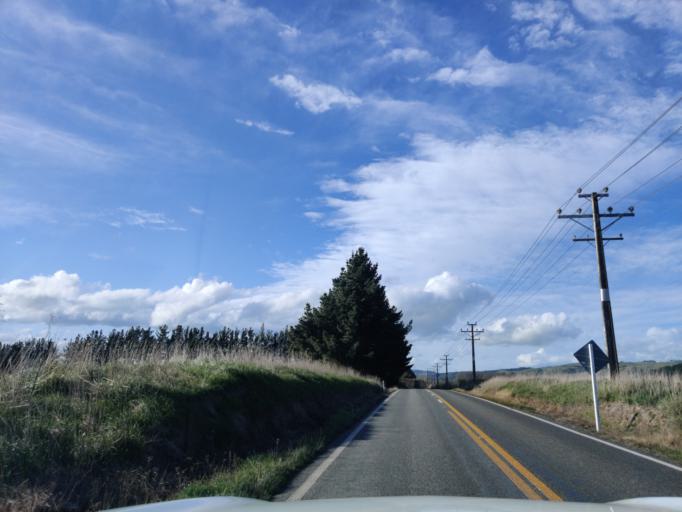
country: NZ
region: Manawatu-Wanganui
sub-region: Palmerston North City
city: Palmerston North
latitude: -40.3373
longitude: 175.7248
